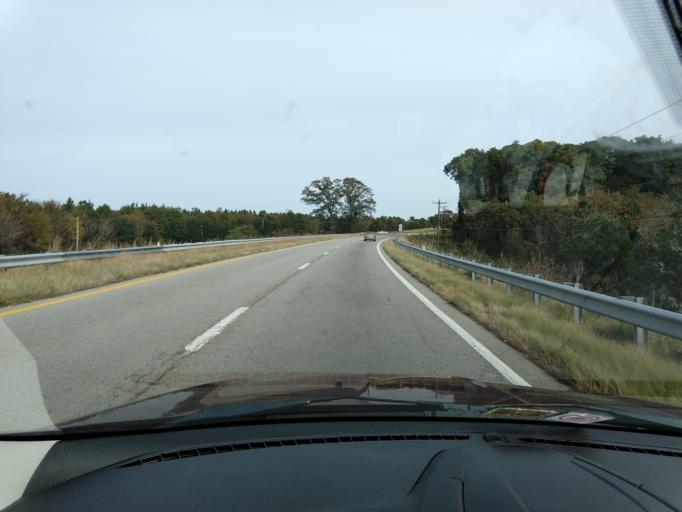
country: US
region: Virginia
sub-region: Pittsylvania County
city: Chatham
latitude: 36.8859
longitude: -79.4057
